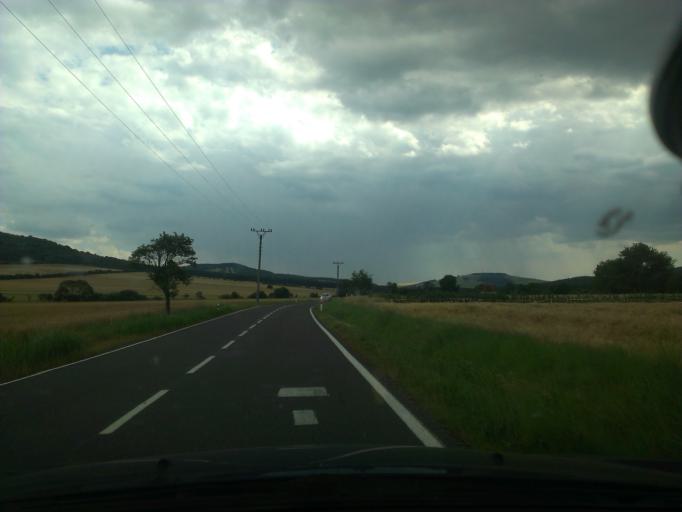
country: CZ
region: South Moravian
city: Velka nad Velickou
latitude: 48.8571
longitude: 17.5227
